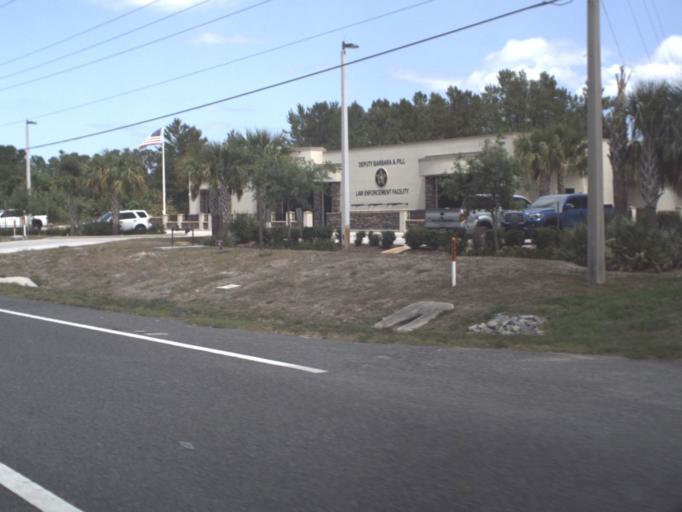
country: US
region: Florida
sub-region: Brevard County
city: Titusville
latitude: 28.5422
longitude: -80.8304
